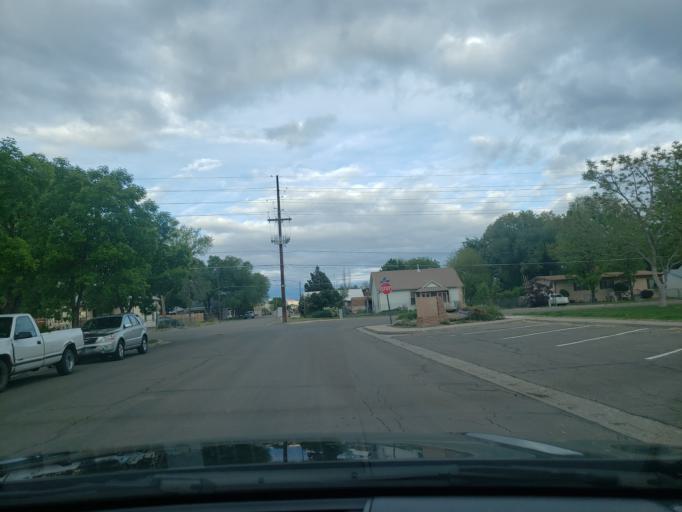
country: US
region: Colorado
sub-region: Mesa County
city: Fruita
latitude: 39.1571
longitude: -108.7295
